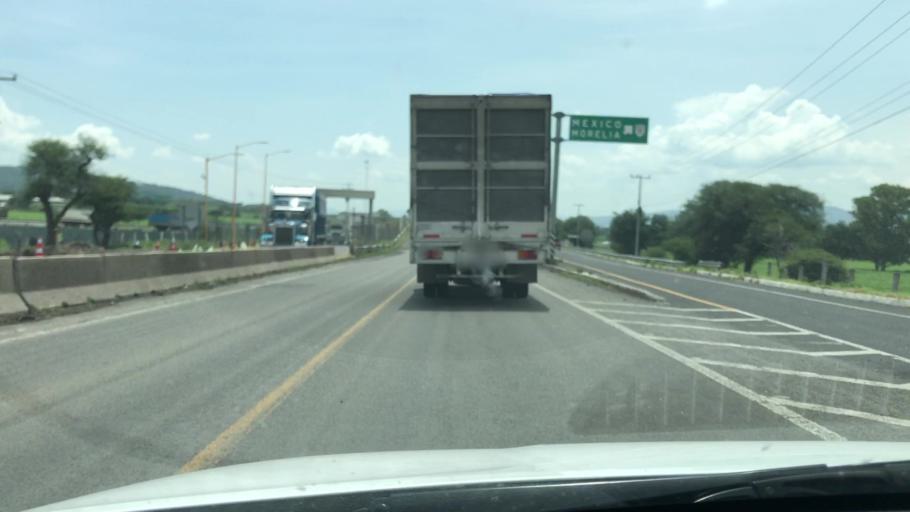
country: MX
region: Michoacan
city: Vistahermosa de Negrete
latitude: 20.2691
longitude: -102.4429
